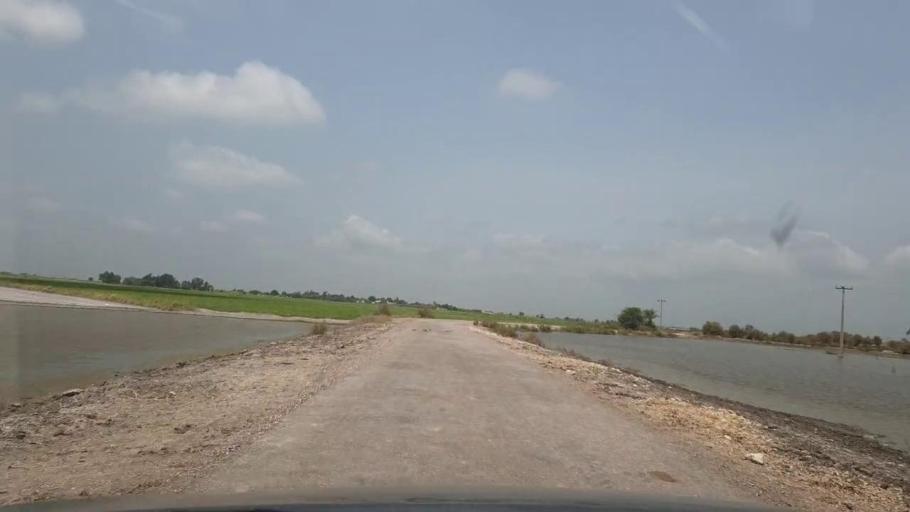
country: PK
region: Sindh
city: Ratodero
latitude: 27.9044
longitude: 68.3145
